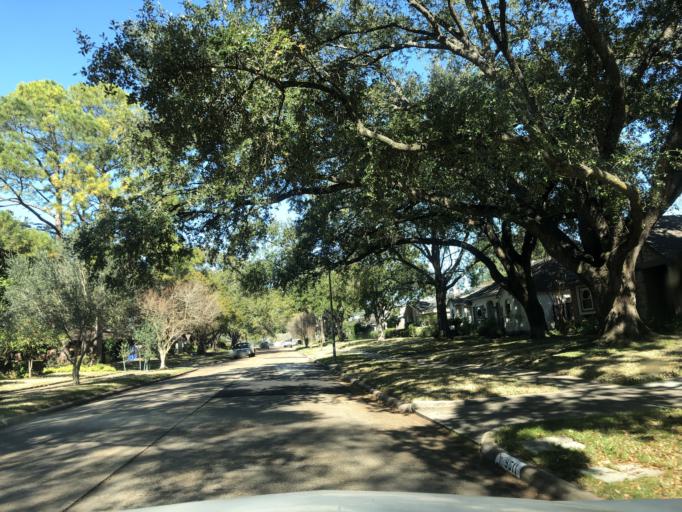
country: US
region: Texas
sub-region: Harris County
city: Bellaire
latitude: 29.6755
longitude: -95.4972
